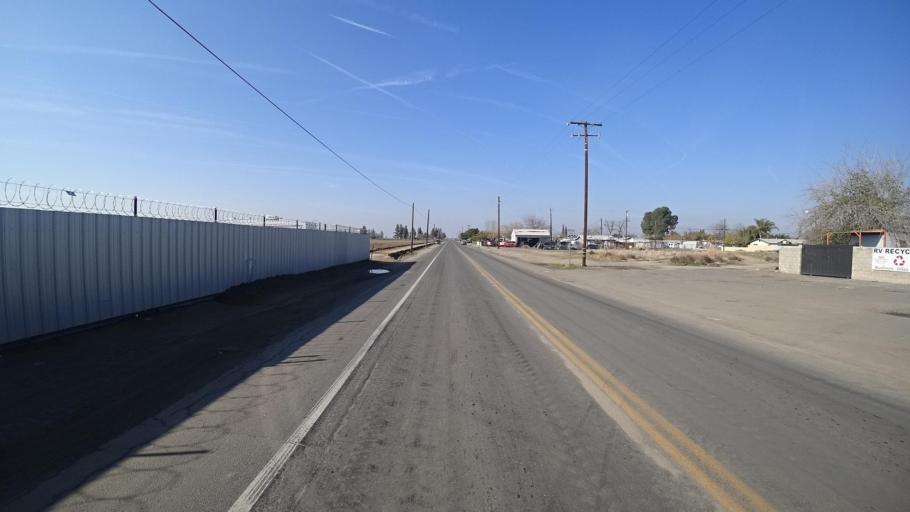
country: US
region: California
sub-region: Kern County
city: Weedpatch
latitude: 35.2378
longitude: -118.9149
